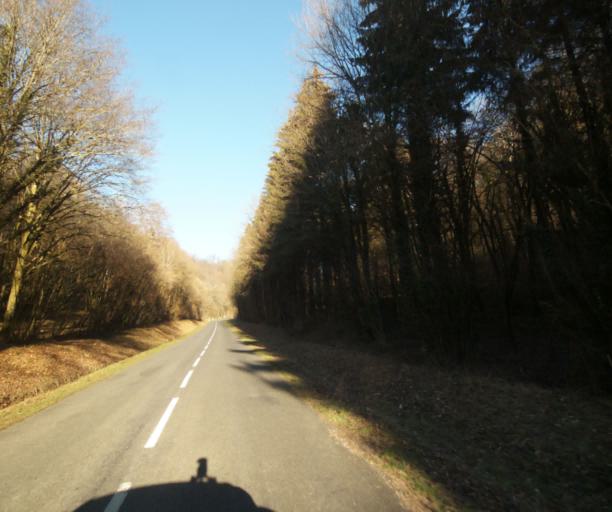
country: FR
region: Champagne-Ardenne
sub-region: Departement de la Haute-Marne
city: Chevillon
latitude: 48.5325
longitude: 5.1831
